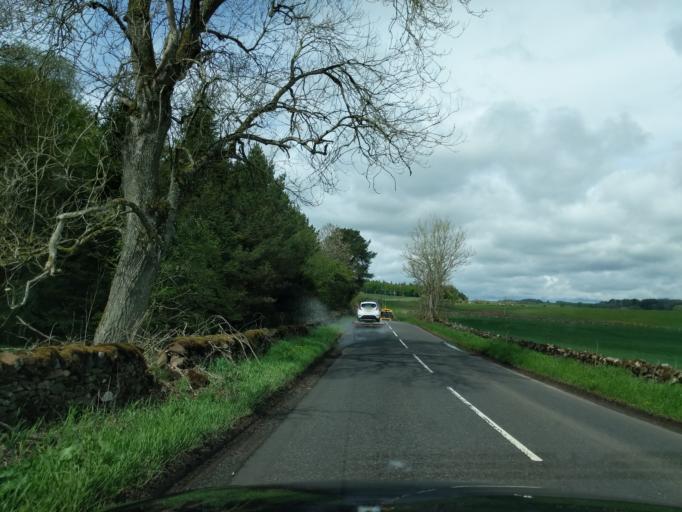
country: GB
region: Scotland
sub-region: The Scottish Borders
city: Earlston
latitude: 55.6929
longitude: -2.5724
